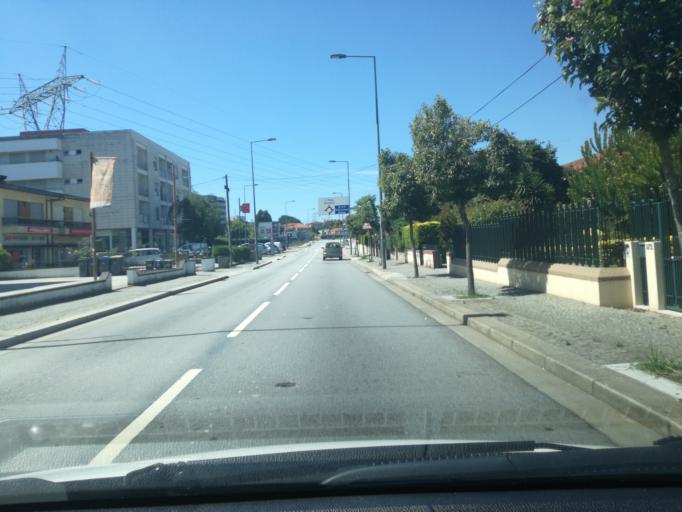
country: PT
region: Porto
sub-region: Maia
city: Nogueira
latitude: 41.2350
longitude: -8.5963
